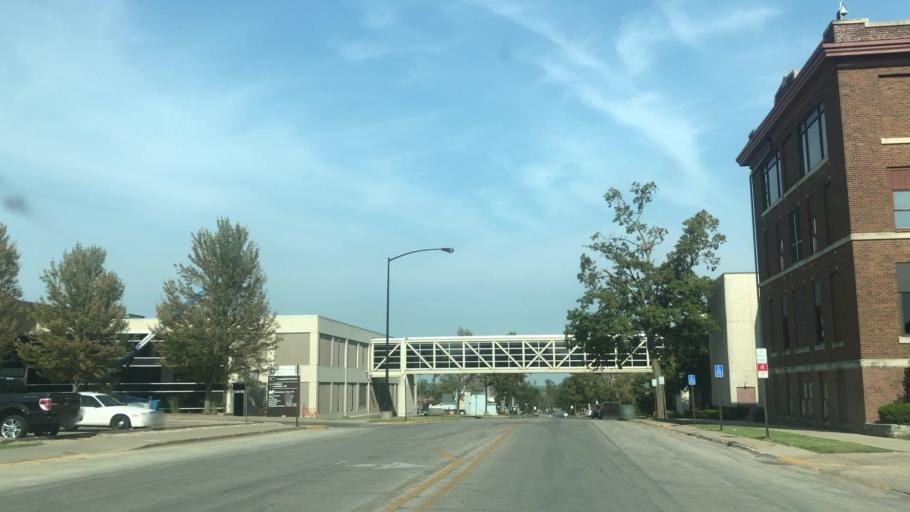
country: US
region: Iowa
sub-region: Marshall County
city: Marshalltown
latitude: 42.0491
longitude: -92.9077
